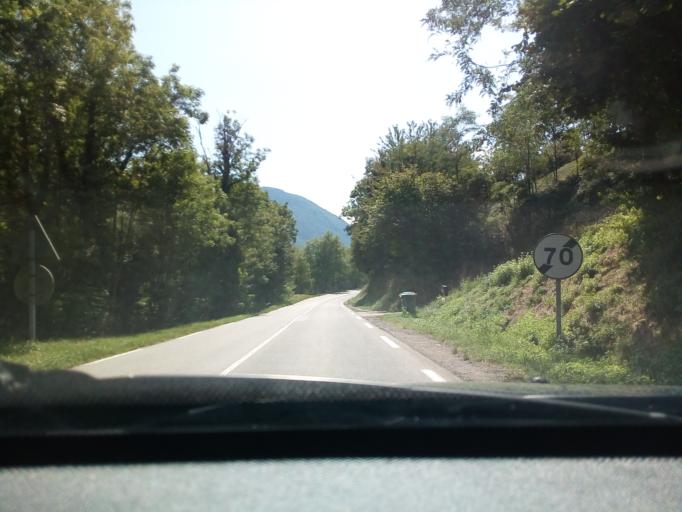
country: FR
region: Rhone-Alpes
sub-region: Departement de l'Isere
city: Brie-et-Angonnes
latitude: 45.1070
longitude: 5.7909
